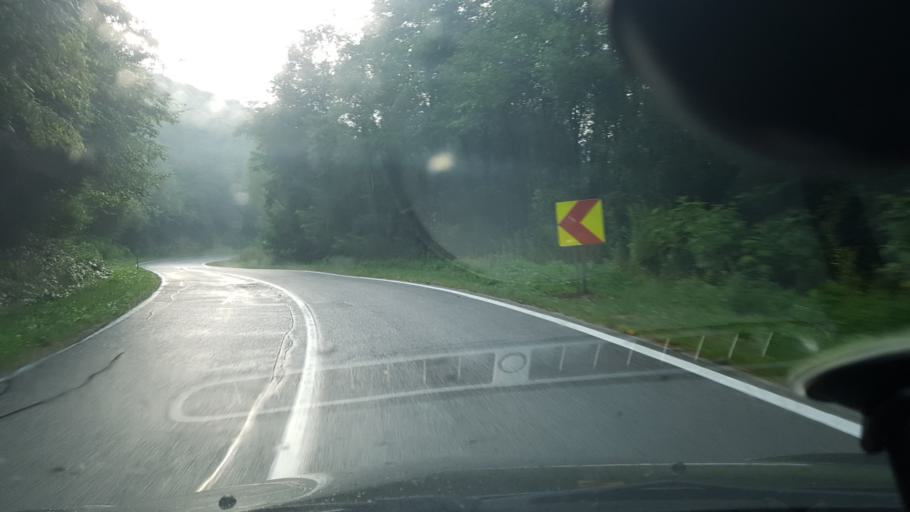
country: SI
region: Rogatec
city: Rogatec
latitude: 46.2203
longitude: 15.7478
